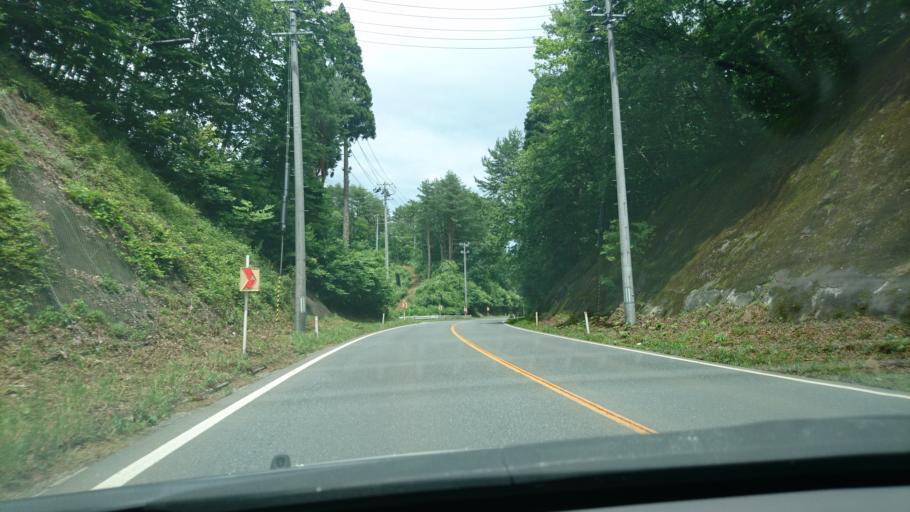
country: JP
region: Iwate
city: Miyako
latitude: 39.7065
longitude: 141.9619
